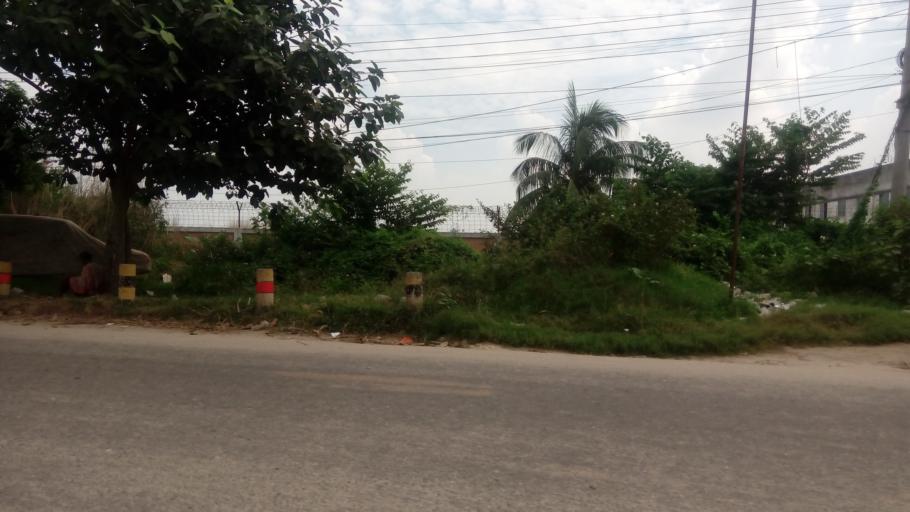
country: BD
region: Dhaka
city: Azimpur
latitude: 23.7467
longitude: 90.3519
